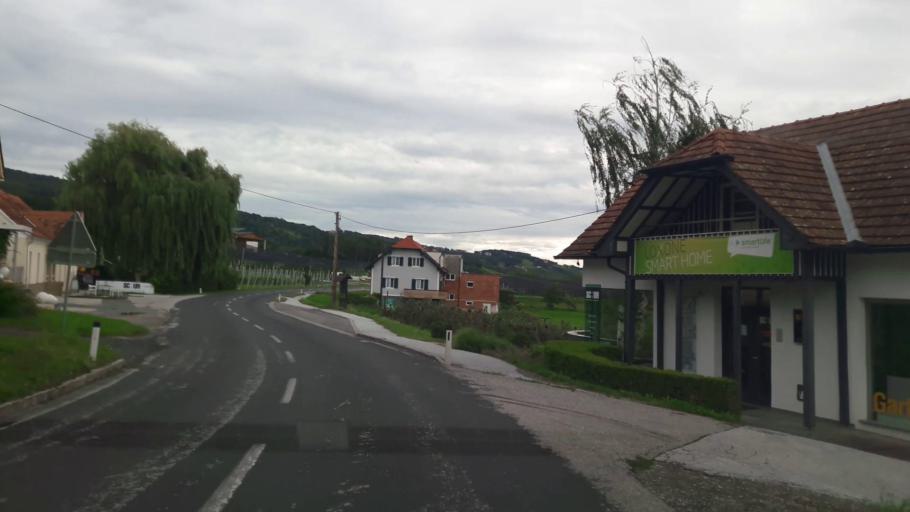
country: AT
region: Styria
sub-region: Politischer Bezirk Hartberg-Fuerstenfeld
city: Stubenberg
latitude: 47.2344
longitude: 15.8223
